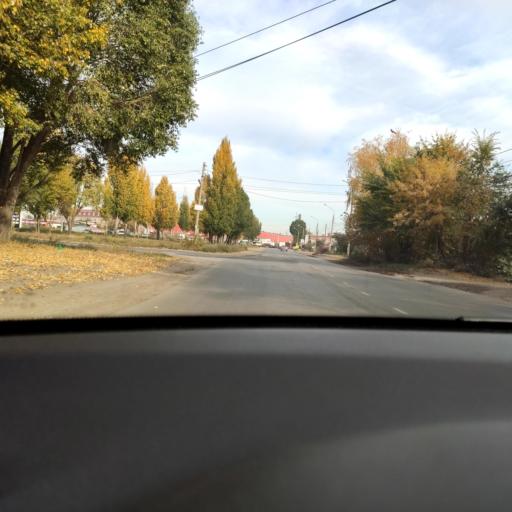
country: RU
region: Samara
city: Petra-Dubrava
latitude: 53.2505
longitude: 50.3101
